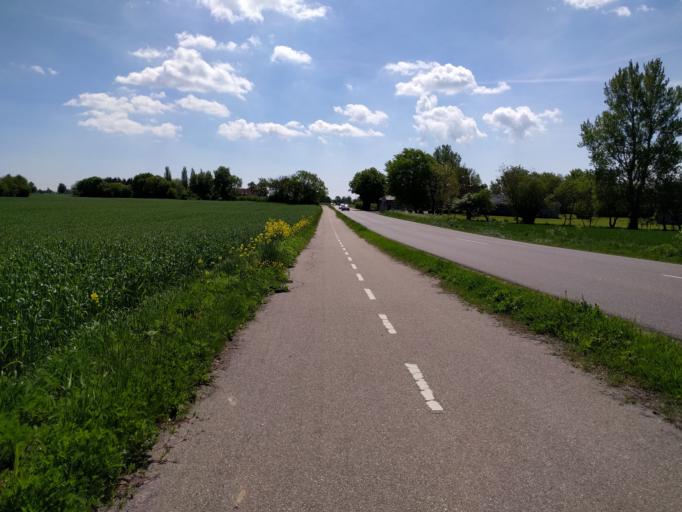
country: DK
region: Zealand
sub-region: Guldborgsund Kommune
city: Nykobing Falster
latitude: 54.7512
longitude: 11.9346
